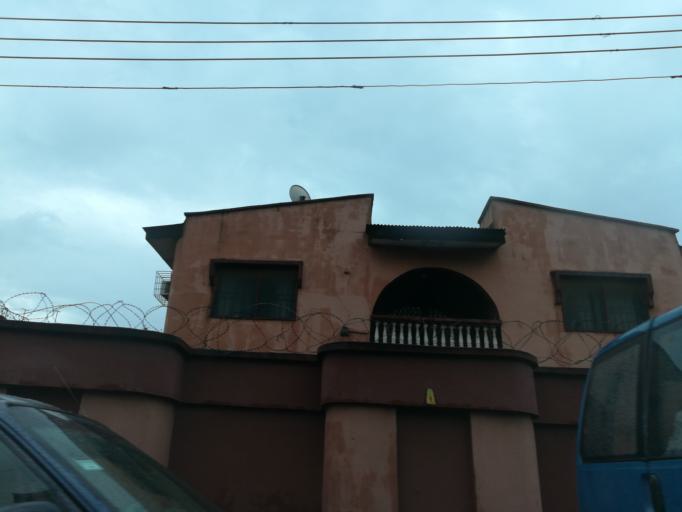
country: NG
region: Lagos
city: Oshodi
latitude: 6.5552
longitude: 3.3441
